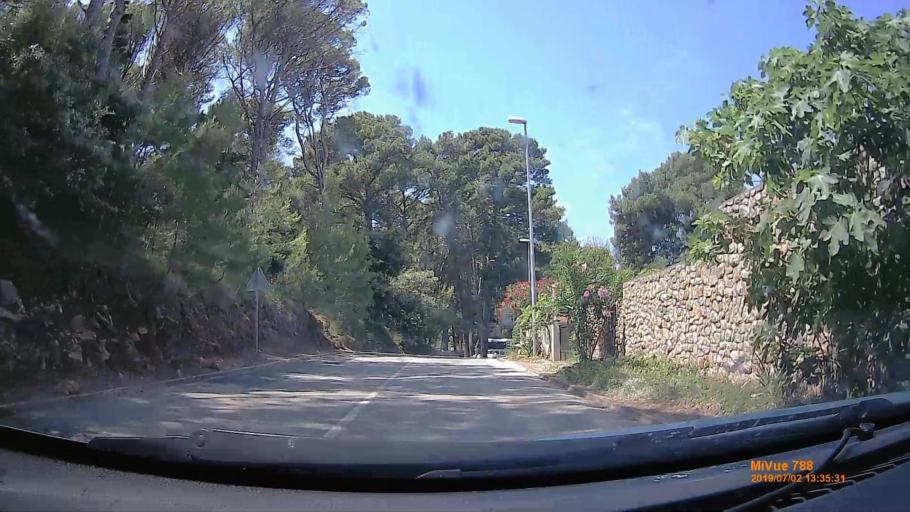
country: HR
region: Primorsko-Goranska
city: Mali Losinj
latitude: 44.5184
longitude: 14.4990
